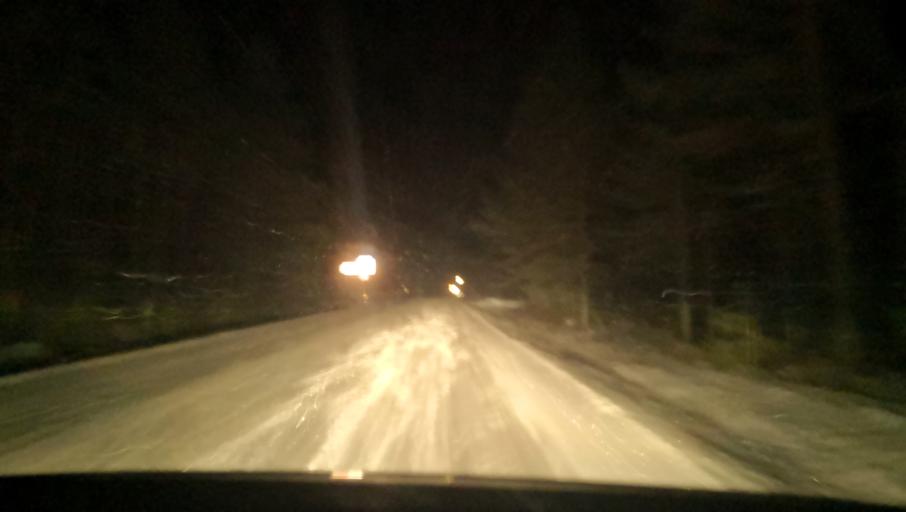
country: SE
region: Uppsala
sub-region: Heby Kommun
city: Tarnsjo
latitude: 60.1365
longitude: 16.9029
